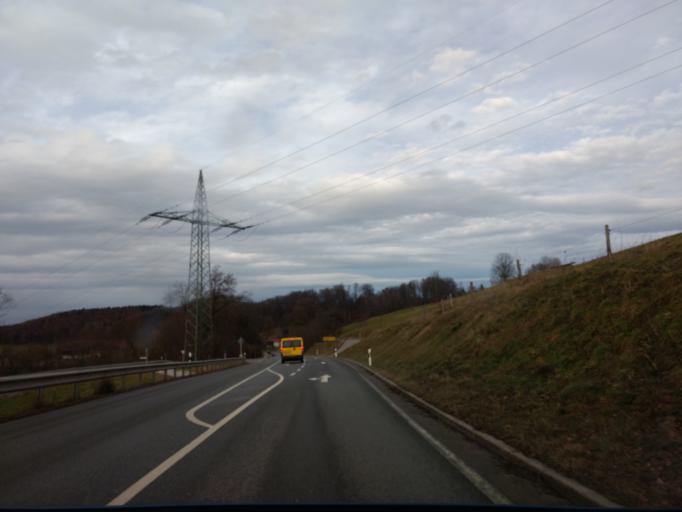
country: DE
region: Bavaria
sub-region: Upper Bavaria
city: Nussdorf
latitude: 47.8751
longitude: 12.5956
